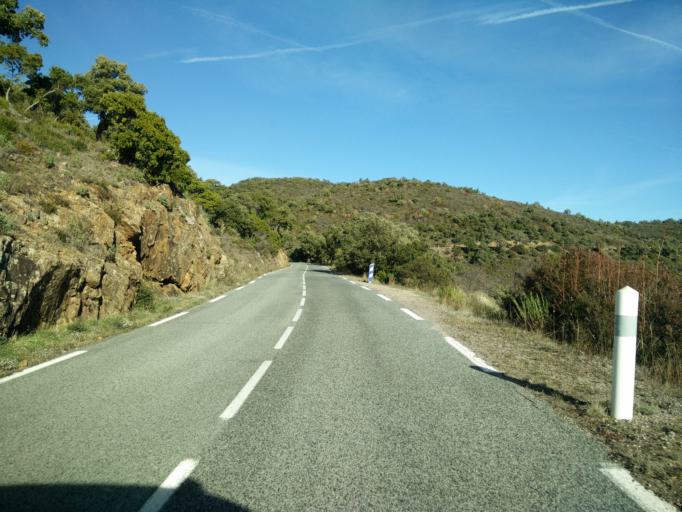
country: FR
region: Provence-Alpes-Cote d'Azur
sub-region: Departement du Var
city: Saint-Raphael
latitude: 43.4978
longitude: 6.7817
